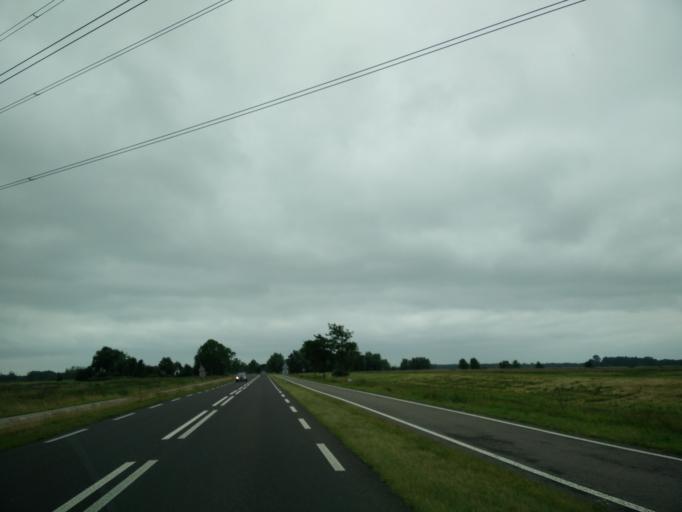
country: NL
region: Groningen
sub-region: Gemeente Groningen
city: Groningen
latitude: 53.1758
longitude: 6.5007
